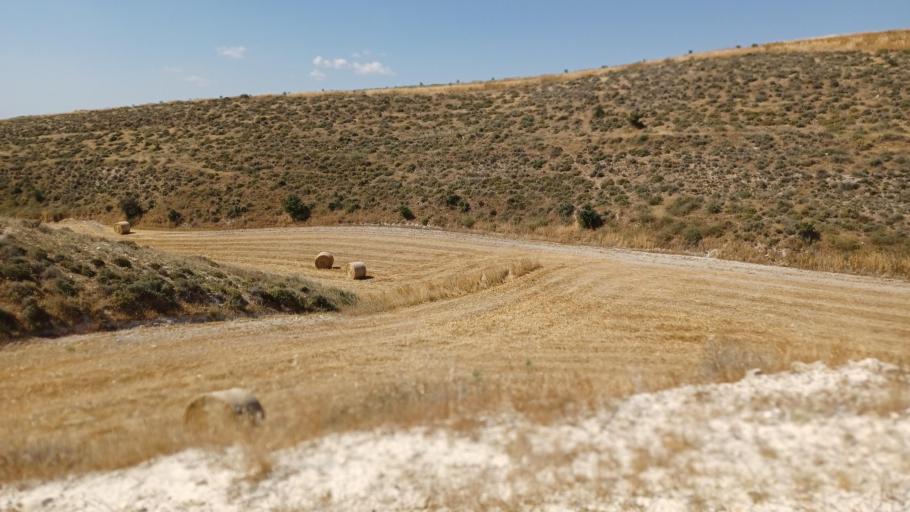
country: CY
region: Larnaka
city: Aradippou
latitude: 34.9942
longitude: 33.5651
